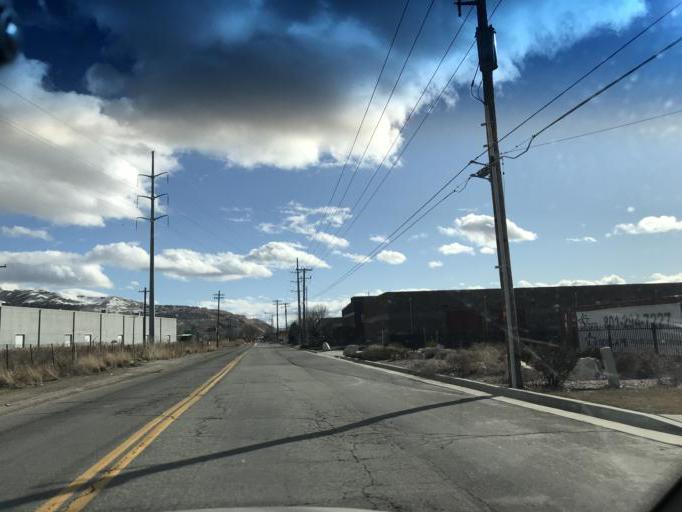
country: US
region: Utah
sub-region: Davis County
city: North Salt Lake
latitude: 40.8588
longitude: -111.9119
